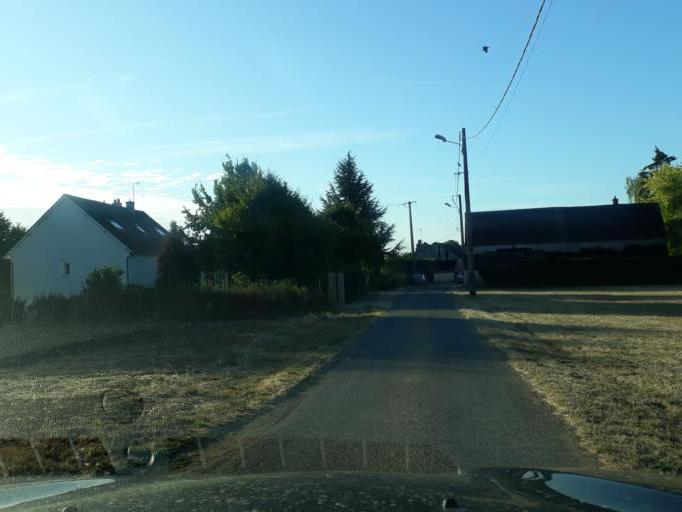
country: FR
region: Centre
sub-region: Departement du Loir-et-Cher
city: Ouzouer-le-Marche
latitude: 47.9715
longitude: 1.5382
